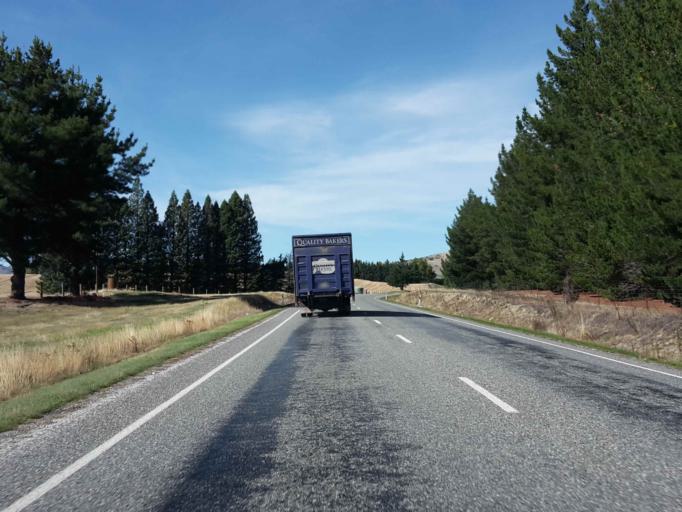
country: NZ
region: Otago
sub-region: Queenstown-Lakes District
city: Wanaka
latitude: -44.7090
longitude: 169.2054
